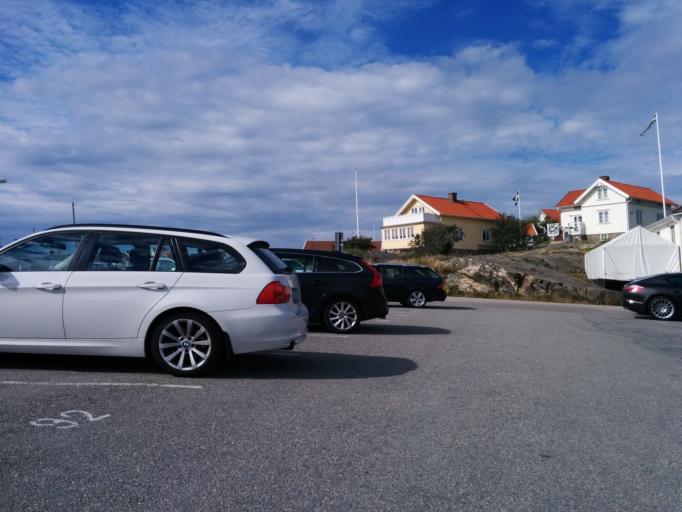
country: SE
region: Vaestra Goetaland
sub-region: Lysekils Kommun
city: Lysekil
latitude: 58.1211
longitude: 11.4441
